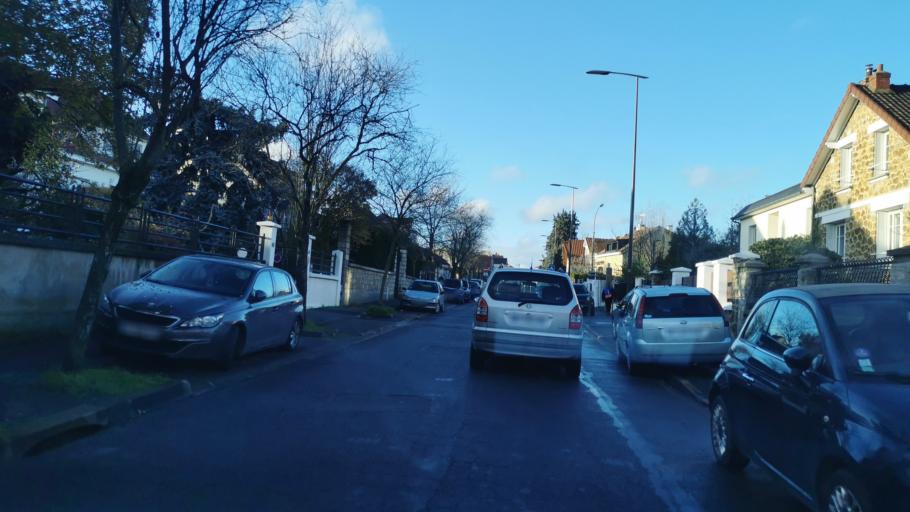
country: FR
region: Ile-de-France
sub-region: Departement de Seine-Saint-Denis
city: Rosny-sous-Bois
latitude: 48.8651
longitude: 2.4906
